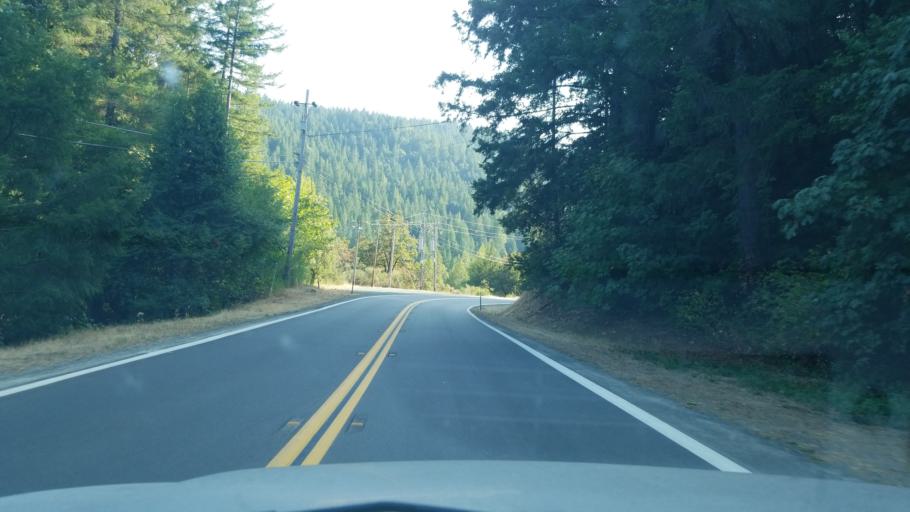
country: US
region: California
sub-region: Humboldt County
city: Redway
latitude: 40.2211
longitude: -123.8081
